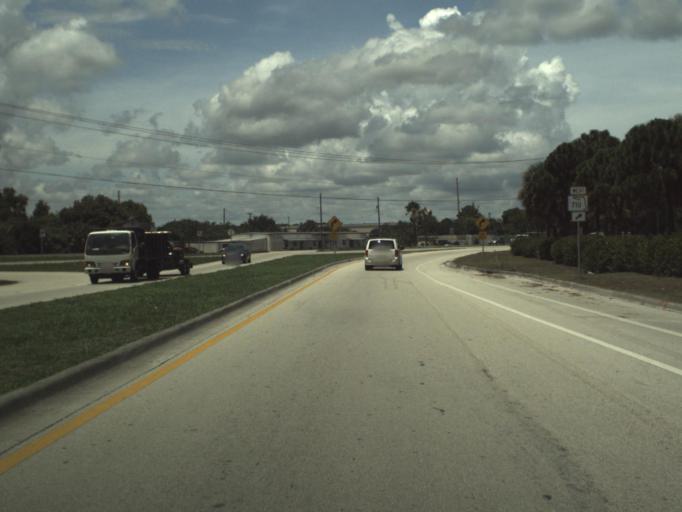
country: US
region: Florida
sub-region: Palm Beach County
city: Mangonia Park
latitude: 26.7837
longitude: -80.1118
